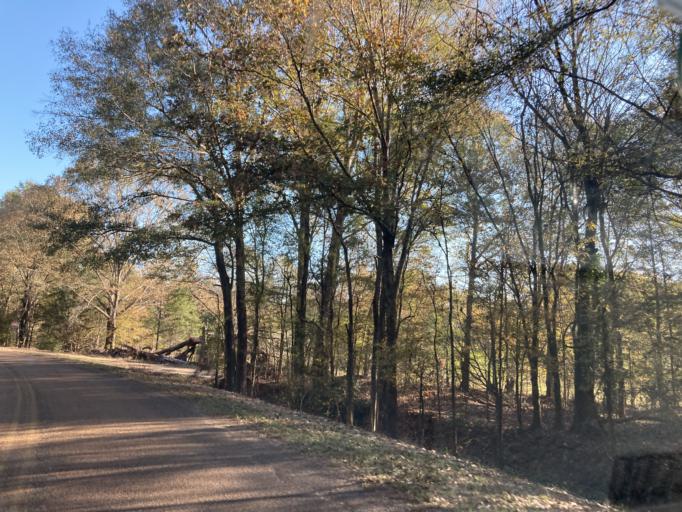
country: US
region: Mississippi
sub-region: Madison County
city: Canton
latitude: 32.7135
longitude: -90.1671
